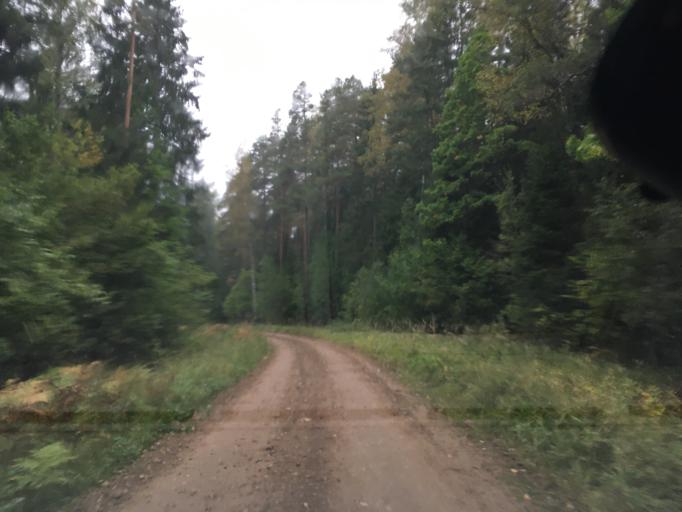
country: LV
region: Kuldigas Rajons
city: Kuldiga
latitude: 56.9873
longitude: 22.0034
